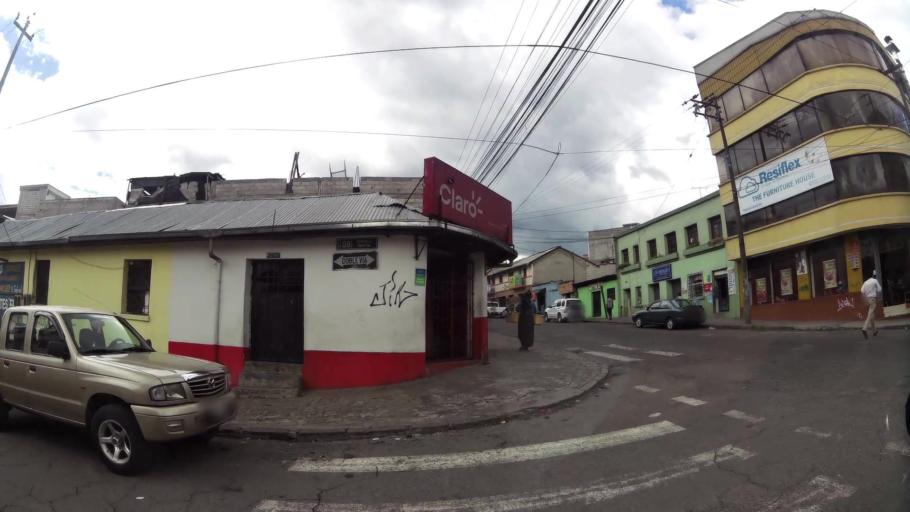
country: EC
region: Pichincha
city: Quito
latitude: -0.2489
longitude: -78.5165
